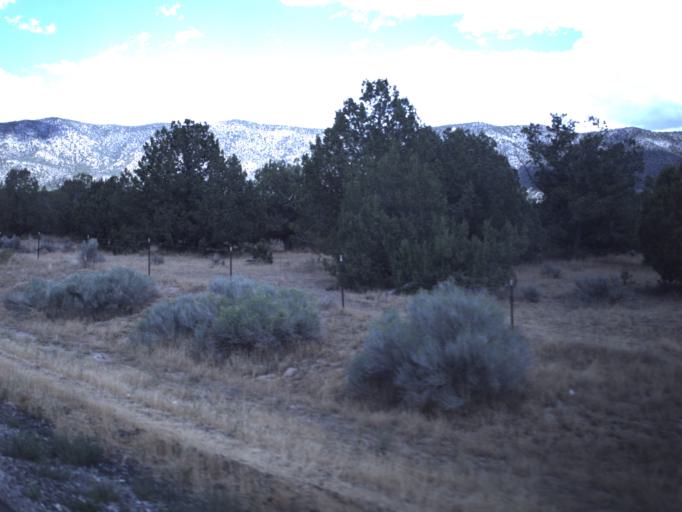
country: US
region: Utah
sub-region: Tooele County
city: Grantsville
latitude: 40.3102
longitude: -112.6383
